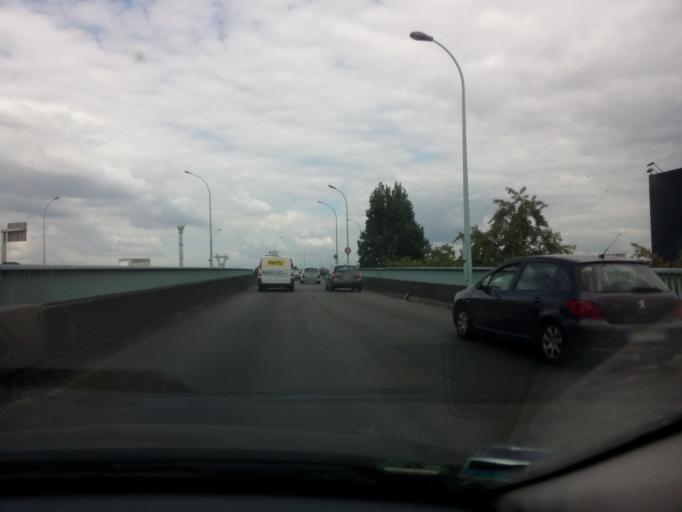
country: FR
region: Ile-de-France
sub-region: Departement du Val-de-Marne
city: Ivry-sur-Seine
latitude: 48.8270
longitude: 2.3925
